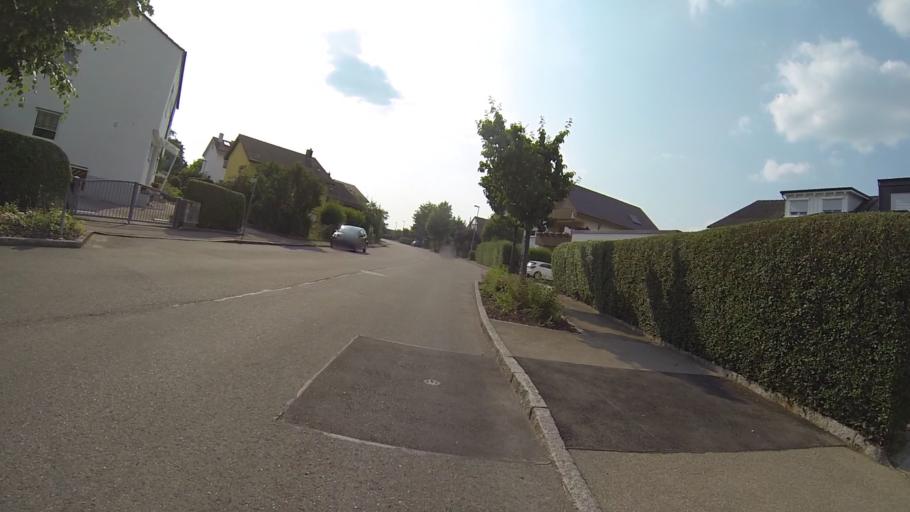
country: DE
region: Baden-Wuerttemberg
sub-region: Tuebingen Region
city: Beimerstetten
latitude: 48.4491
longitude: 9.9932
